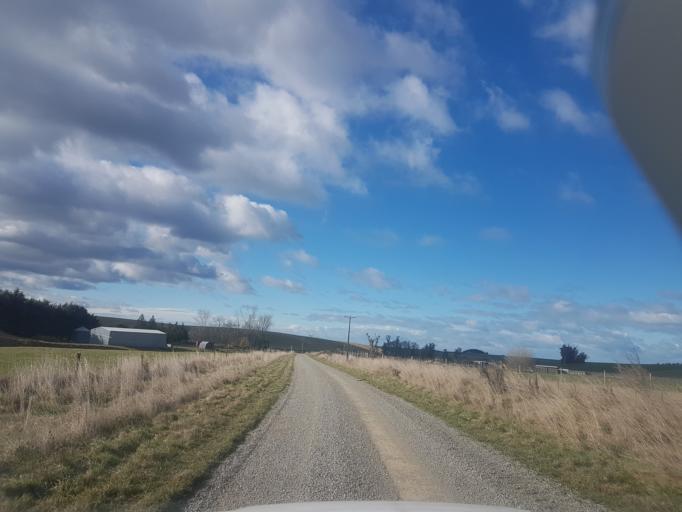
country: NZ
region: Canterbury
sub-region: Timaru District
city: Pleasant Point
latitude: -44.1887
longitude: 171.1811
